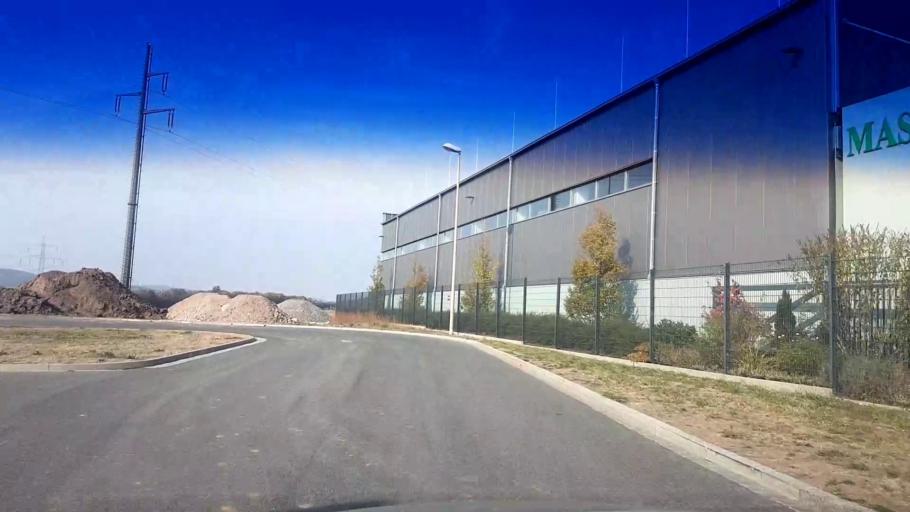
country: DE
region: Bavaria
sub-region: Upper Franconia
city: Viereth-Trunstadt
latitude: 49.9369
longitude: 10.7793
